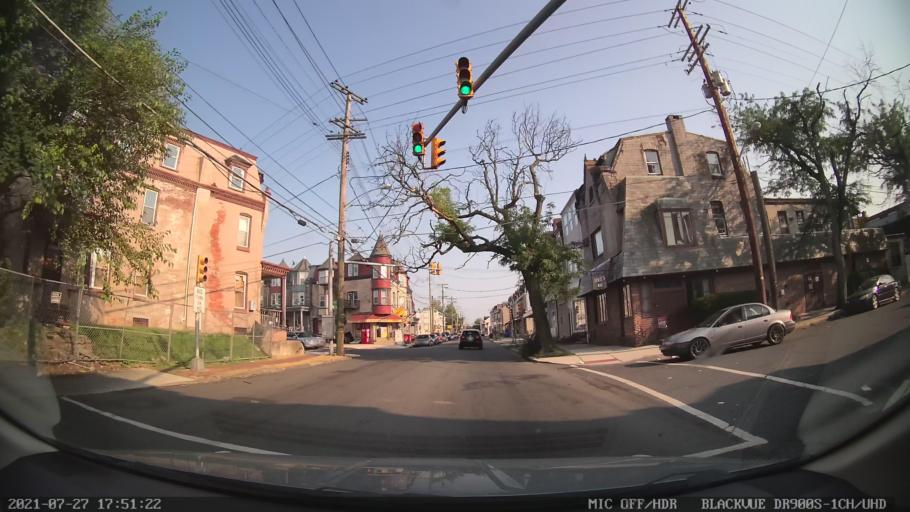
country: US
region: Pennsylvania
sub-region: Berks County
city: West Reading
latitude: 40.3464
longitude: -75.9409
